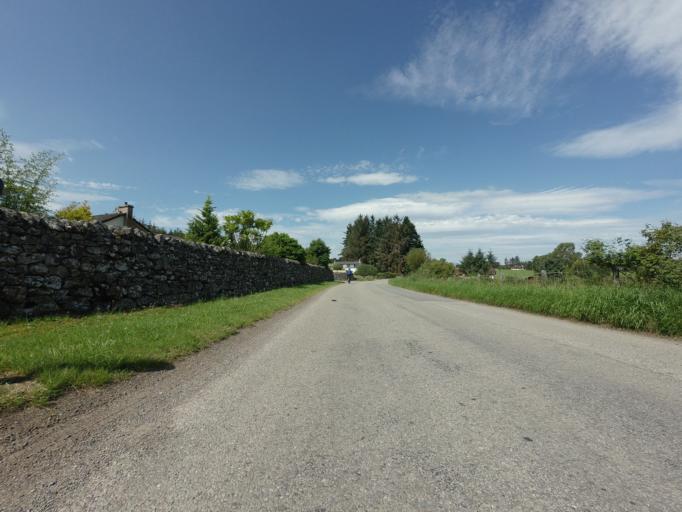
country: GB
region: Scotland
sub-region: Highland
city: Inverness
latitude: 57.5231
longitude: -4.3129
